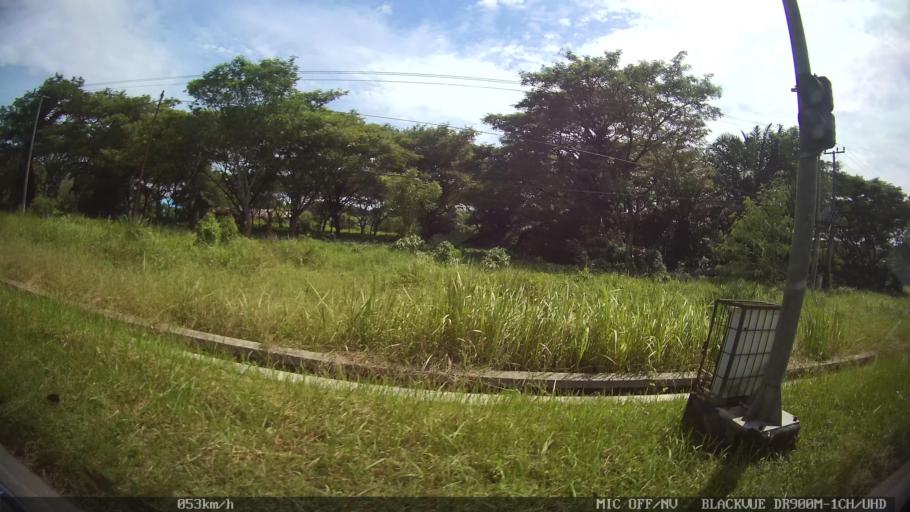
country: ID
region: North Sumatra
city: Percut
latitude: 3.6092
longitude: 98.8557
